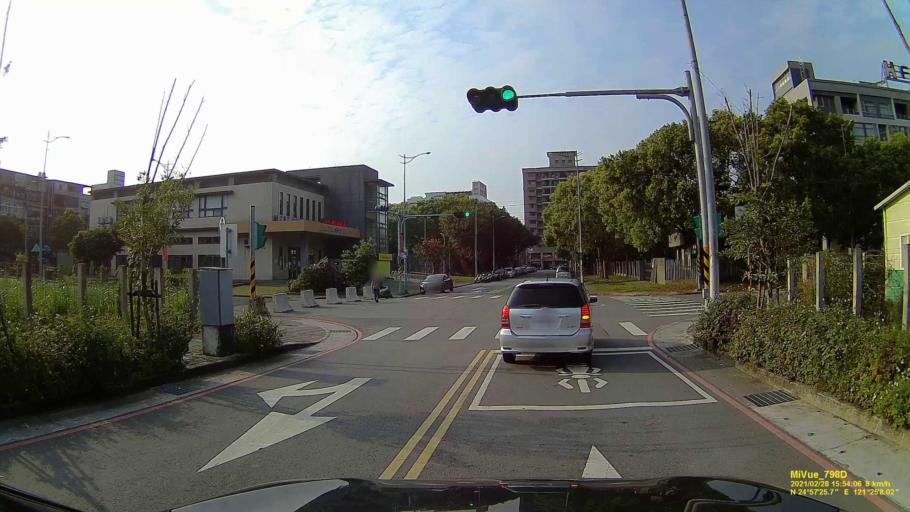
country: TW
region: Taipei
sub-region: Taipei
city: Banqiao
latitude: 24.9572
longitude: 121.4190
